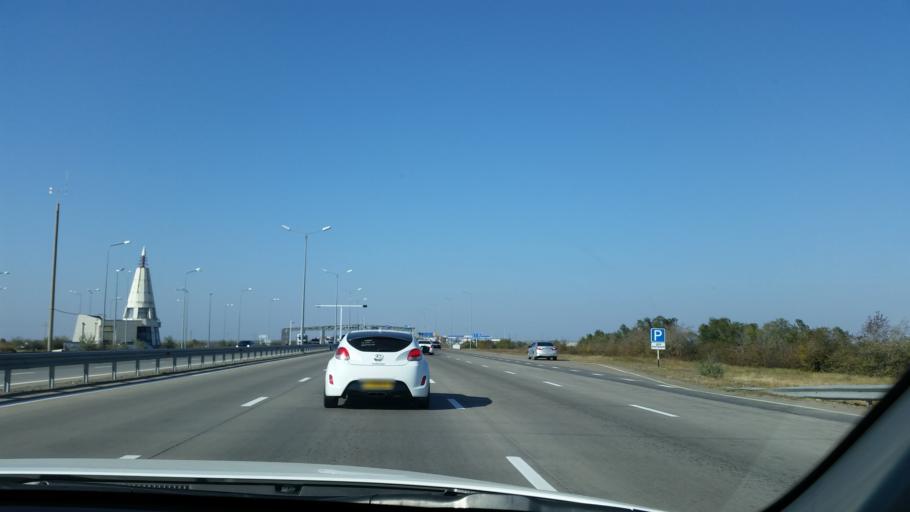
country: KZ
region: Astana Qalasy
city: Astana
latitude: 51.2631
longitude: 71.3709
